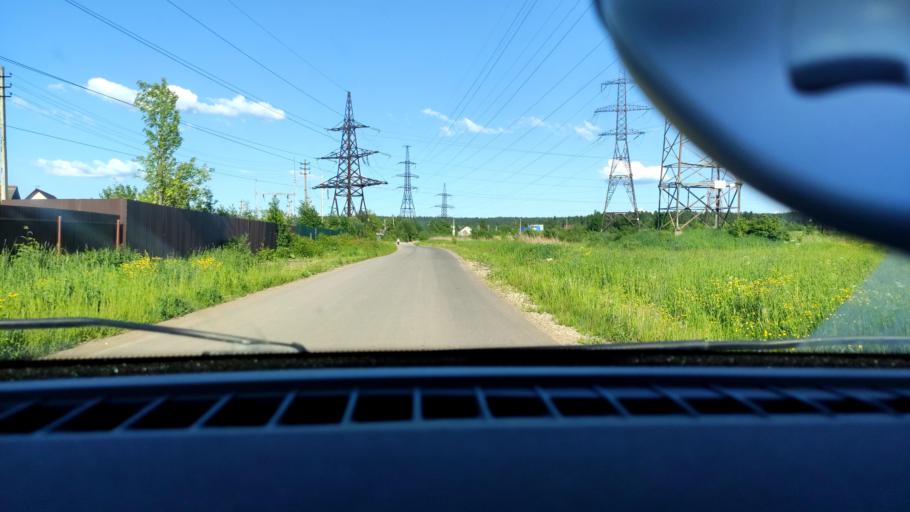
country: RU
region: Perm
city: Ferma
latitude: 57.9159
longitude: 56.3496
